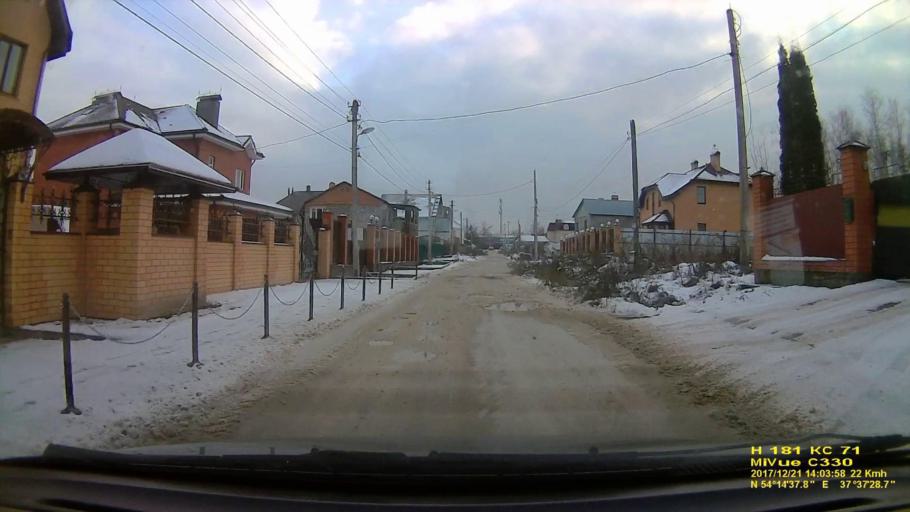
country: RU
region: Tula
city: Gorelki
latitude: 54.2438
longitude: 37.6247
